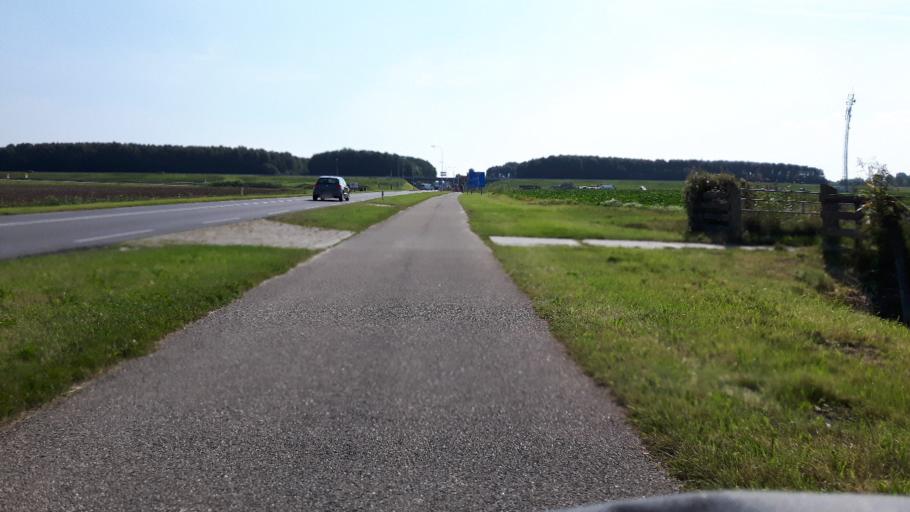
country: NL
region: Friesland
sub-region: Gemeente Franekeradeel
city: Franeker
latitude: 53.2043
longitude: 5.5420
